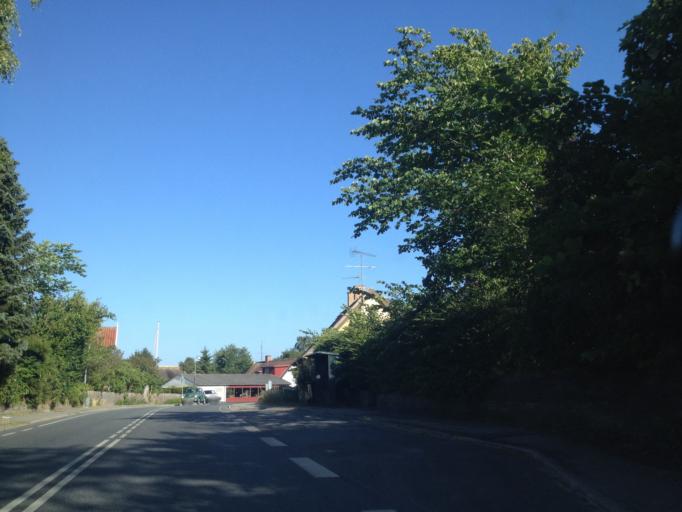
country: DK
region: Capital Region
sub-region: Gribskov Kommune
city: Helsinge
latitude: 56.0517
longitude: 12.1079
